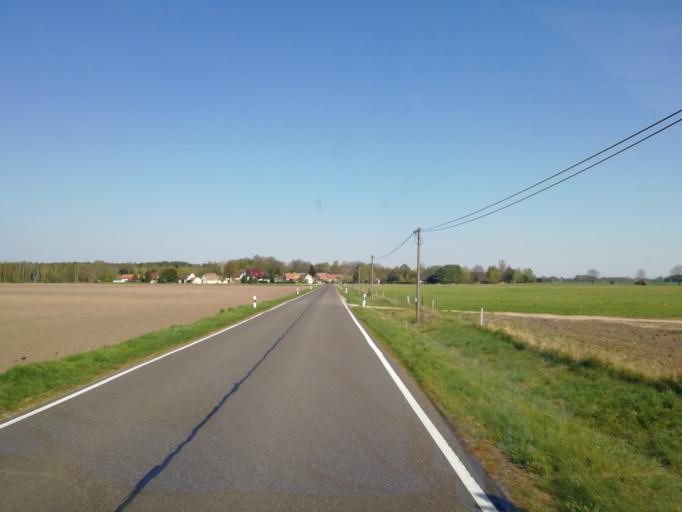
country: DE
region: Brandenburg
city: Crinitz
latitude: 51.7336
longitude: 13.8524
